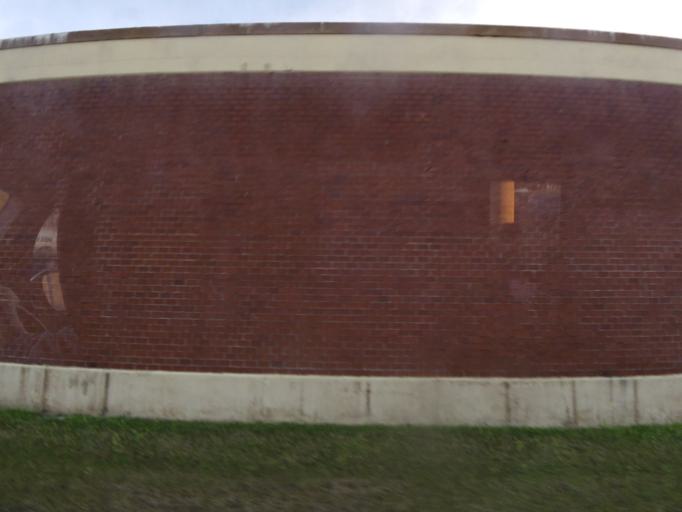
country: US
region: Florida
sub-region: Duval County
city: Jacksonville
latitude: 30.3477
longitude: -81.7118
